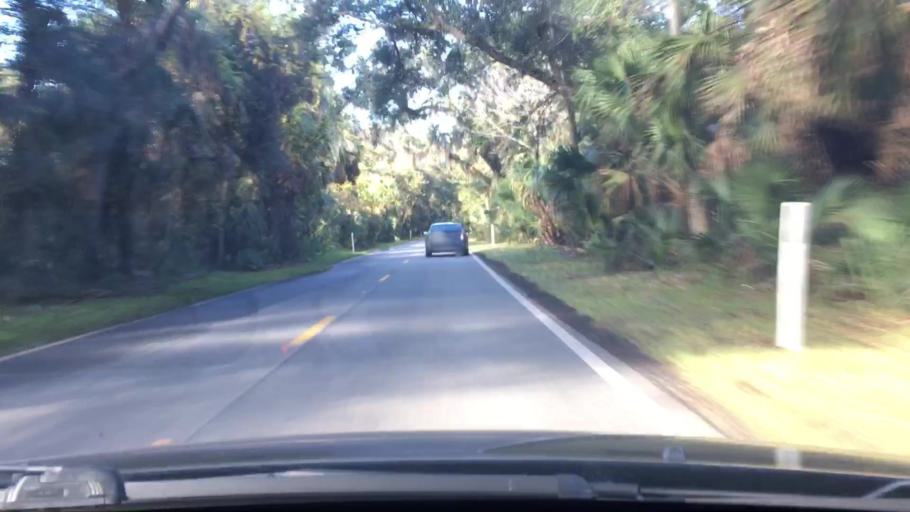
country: US
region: Florida
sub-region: Volusia County
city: Ormond-by-the-Sea
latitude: 29.3932
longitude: -81.1341
